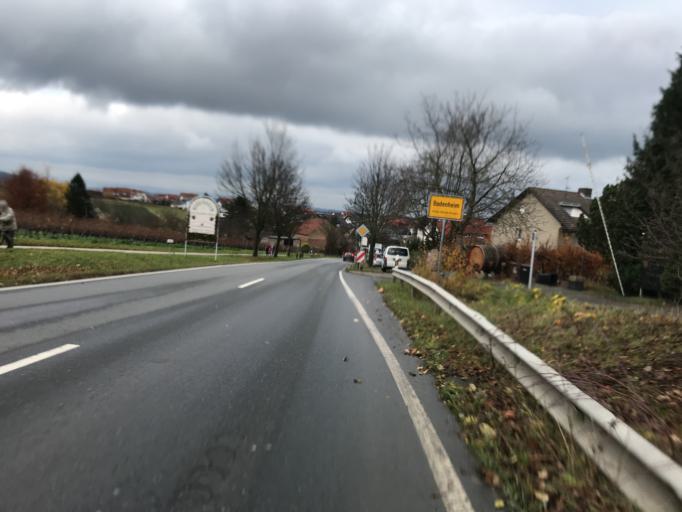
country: DE
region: Rheinland-Pfalz
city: Bodenheim
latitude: 49.9240
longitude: 8.3001
